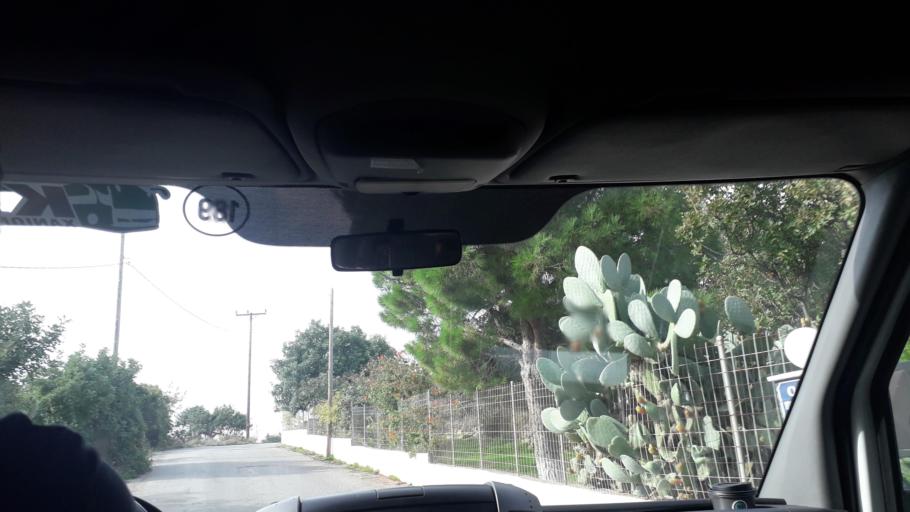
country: GR
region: Crete
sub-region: Nomos Rethymnis
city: Atsipopoulon
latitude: 35.3606
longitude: 24.4327
